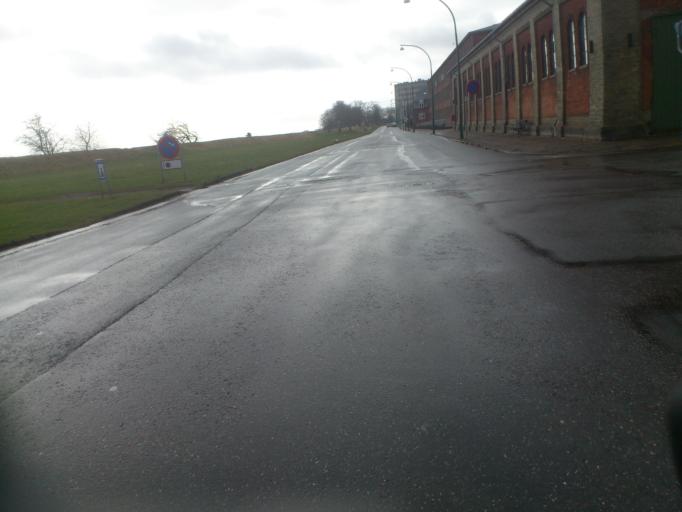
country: DK
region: South Denmark
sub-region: Fredericia Kommune
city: Fredericia
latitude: 55.5670
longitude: 9.7676
